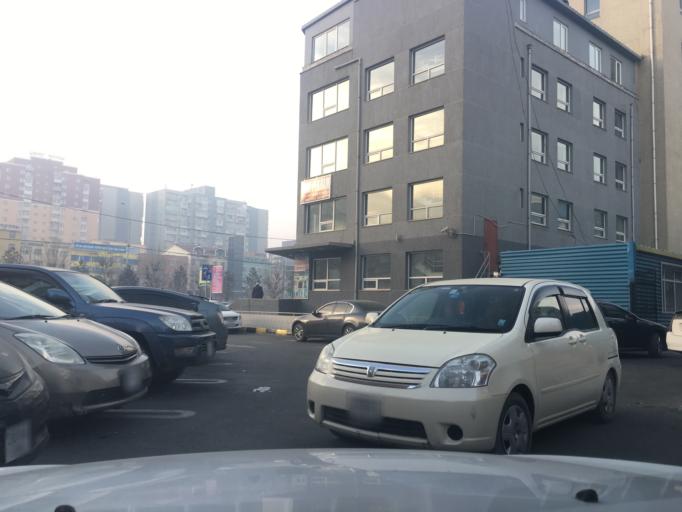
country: MN
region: Ulaanbaatar
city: Ulaanbaatar
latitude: 47.9145
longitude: 106.8666
